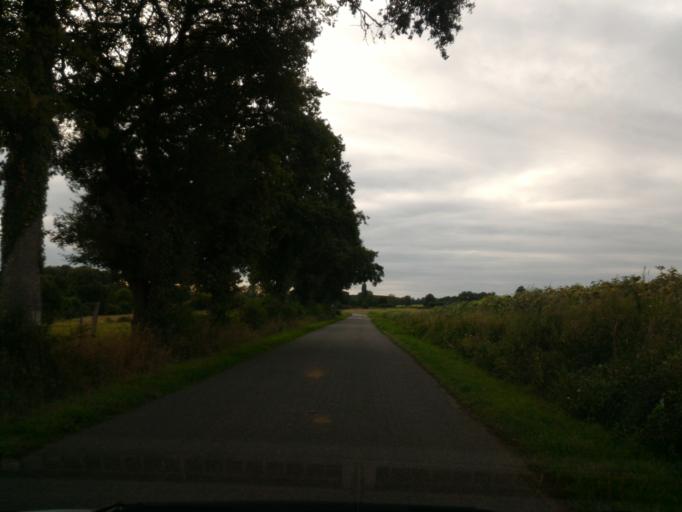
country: FR
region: Poitou-Charentes
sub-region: Departement de la Charente
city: Brigueuil
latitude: 45.9261
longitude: 0.8340
